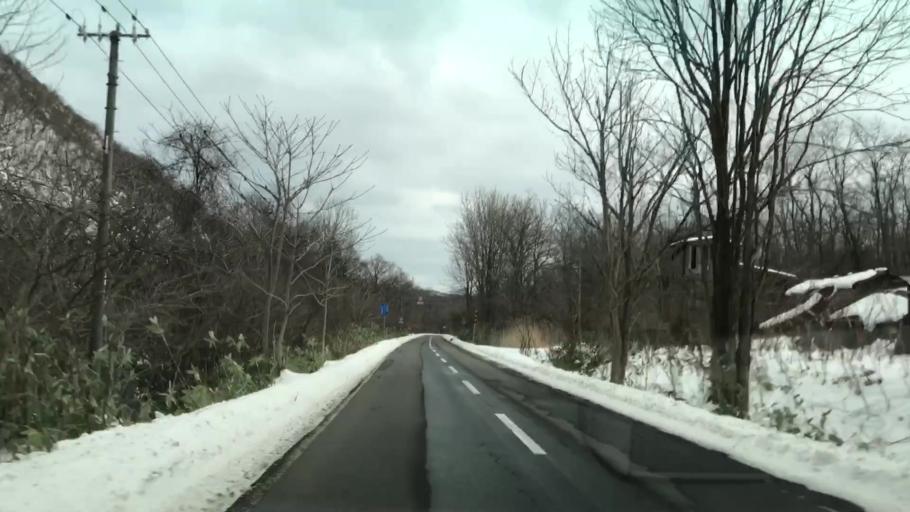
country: JP
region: Hokkaido
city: Yoichi
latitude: 43.3310
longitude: 140.4762
